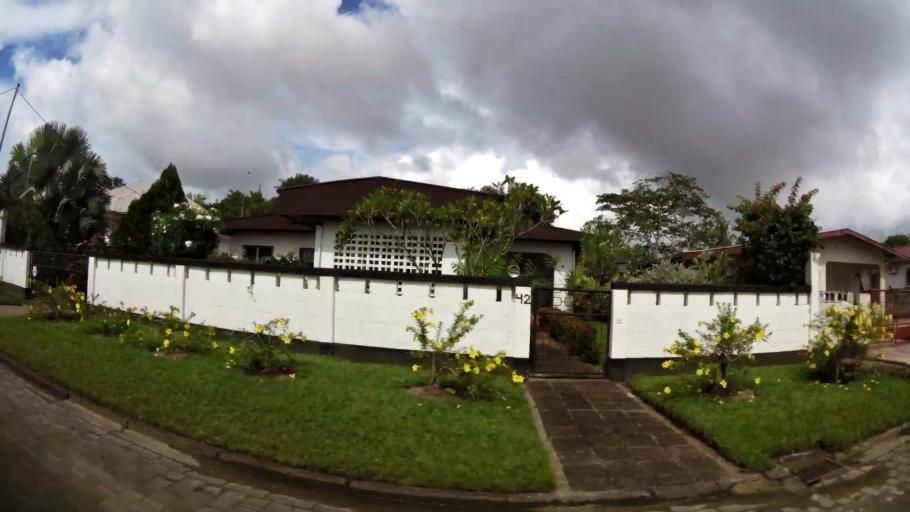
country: SR
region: Paramaribo
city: Paramaribo
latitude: 5.8459
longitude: -55.1909
